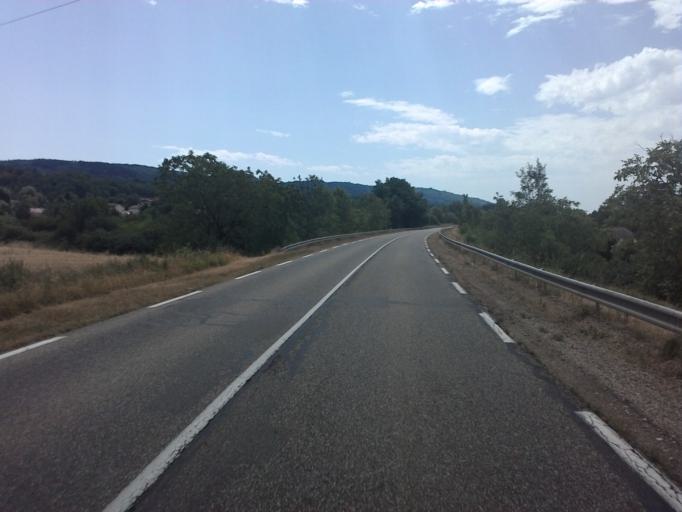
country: FR
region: Franche-Comte
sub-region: Departement du Jura
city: Saint-Amour
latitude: 46.4366
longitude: 5.3537
